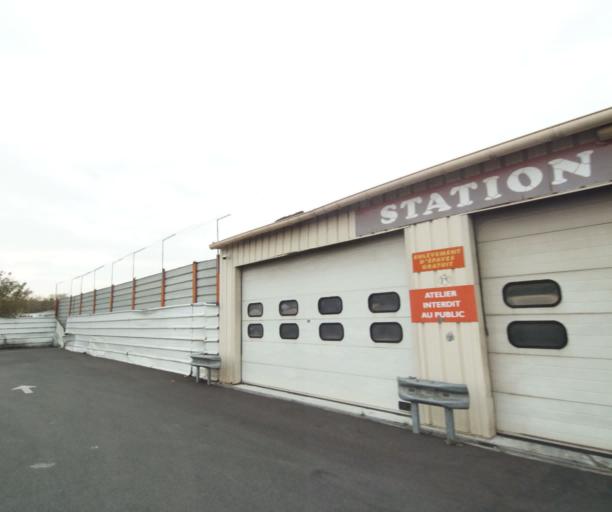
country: FR
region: Ile-de-France
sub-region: Departement de Seine-Saint-Denis
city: Le Blanc-Mesnil
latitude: 48.9633
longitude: 2.4640
